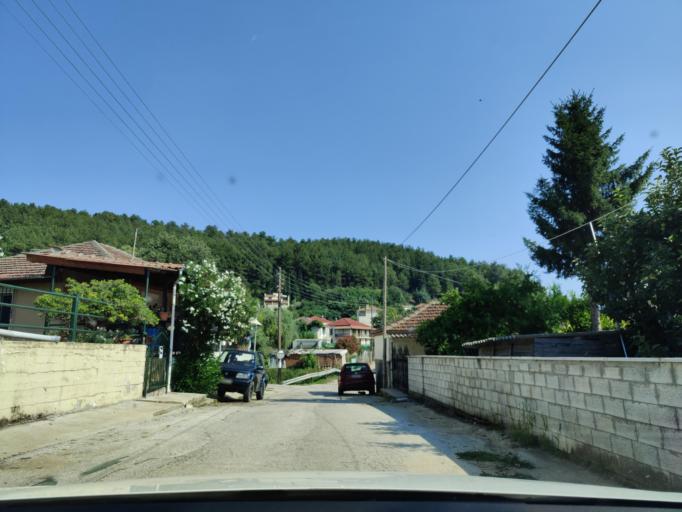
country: GR
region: East Macedonia and Thrace
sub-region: Nomos Kavalas
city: Zygos
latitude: 41.0177
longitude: 24.3835
